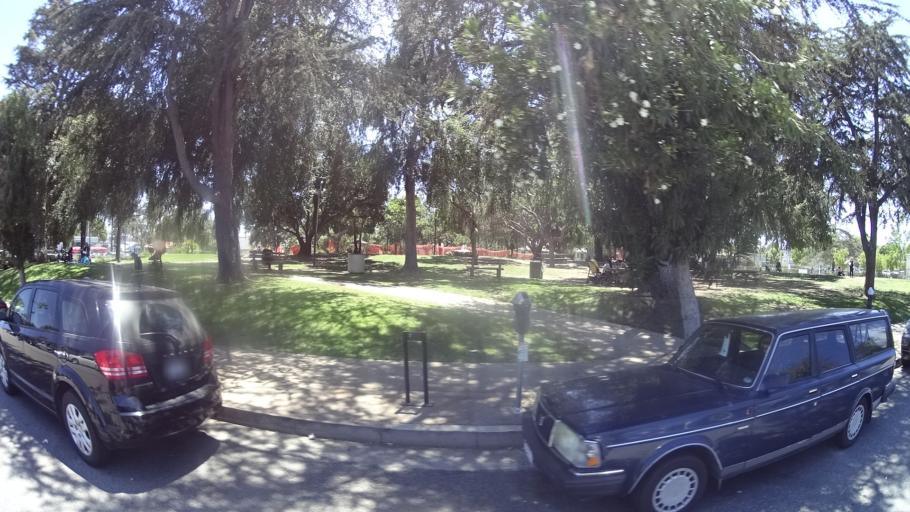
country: US
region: California
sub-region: Los Angeles County
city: Santa Monica
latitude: 34.0361
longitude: -118.4792
